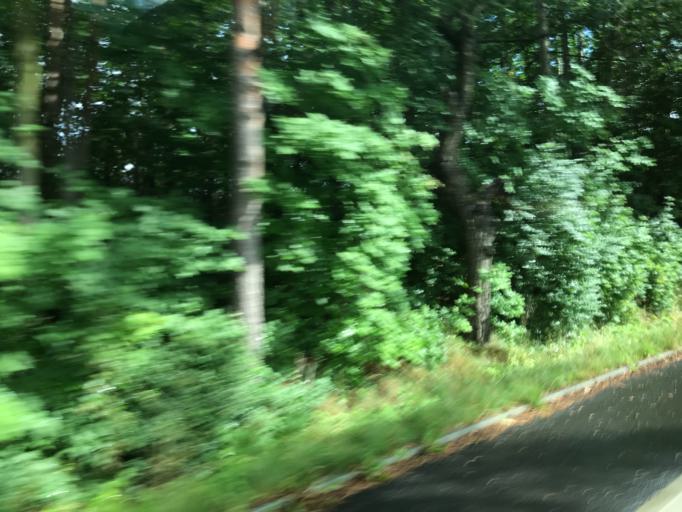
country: CZ
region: Jihocesky
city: Kamenny Ujezd
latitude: 48.9043
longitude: 14.4499
